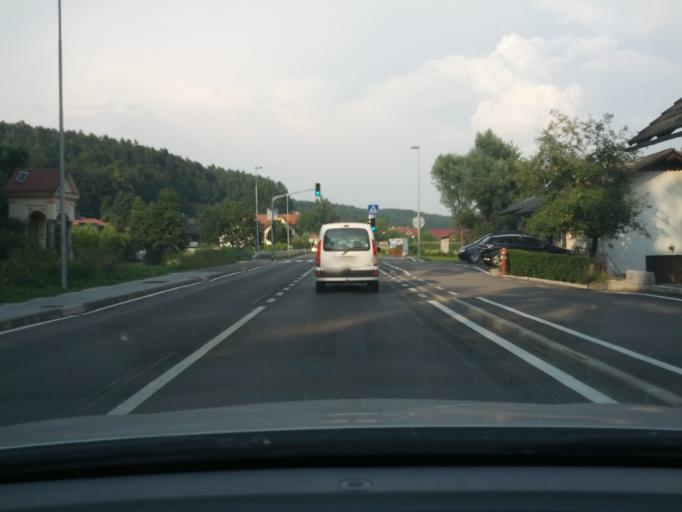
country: SI
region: Brezovica
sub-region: Opstina Ljubljana-Vic-Rudnik
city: Brezovica pri Ljubljani
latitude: 46.0198
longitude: 14.3971
